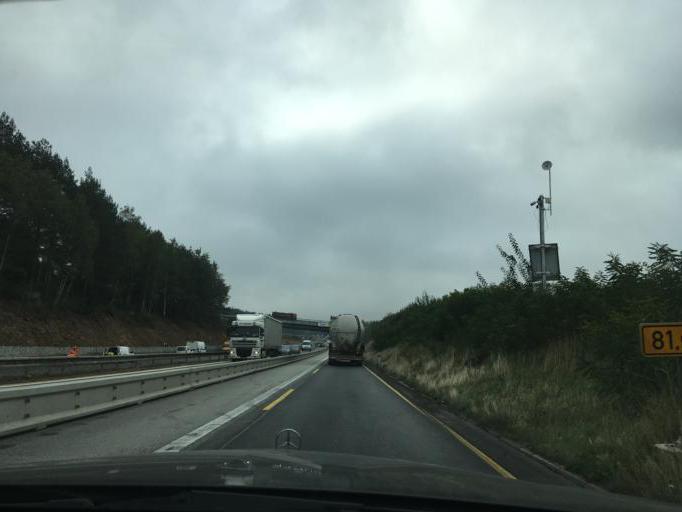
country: CZ
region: Vysocina
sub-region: Okres Pelhrimov
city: Zeliv
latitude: 49.5800
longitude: 15.2630
